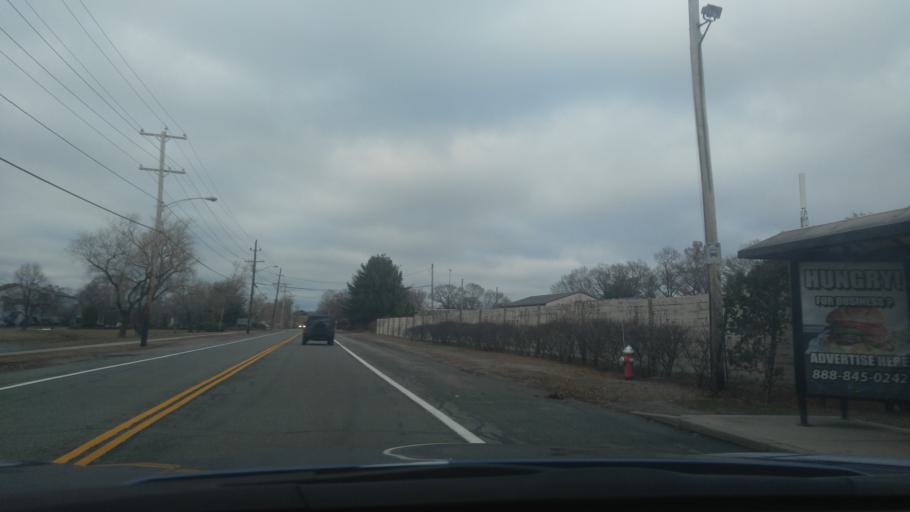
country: US
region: Rhode Island
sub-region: Kent County
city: Warwick
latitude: 41.7052
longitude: -71.3984
